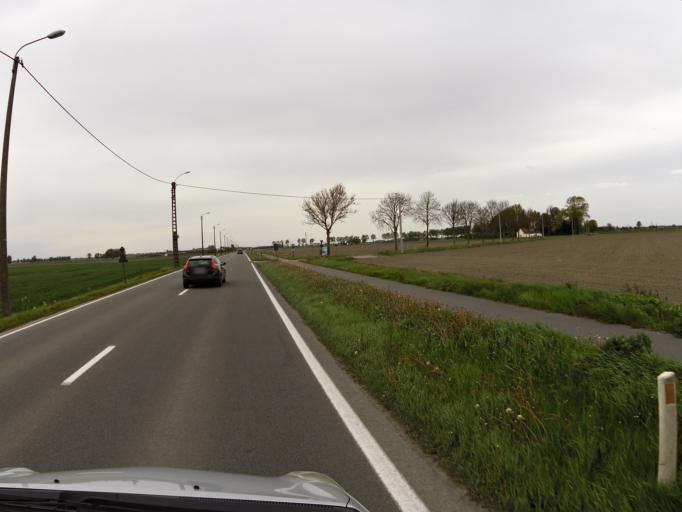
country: BE
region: Flanders
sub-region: Provincie West-Vlaanderen
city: Middelkerke
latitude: 51.1294
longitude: 2.8723
